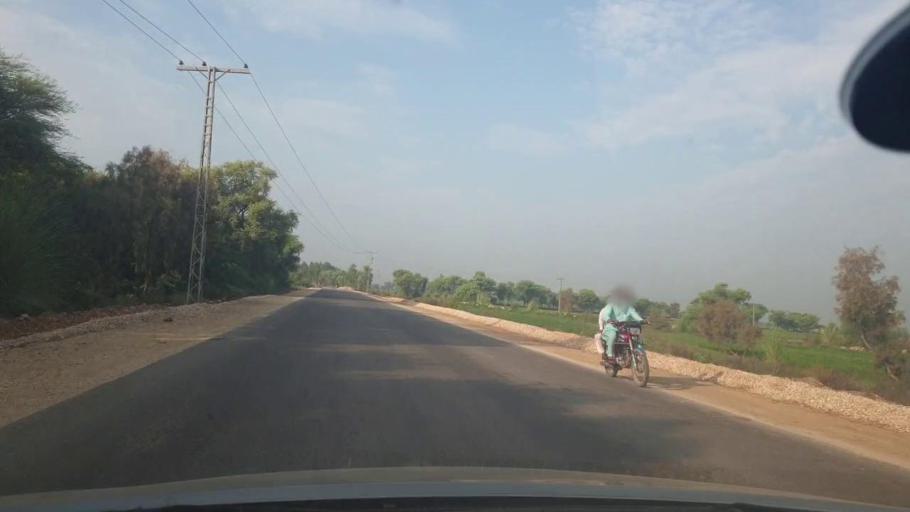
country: PK
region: Sindh
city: Jacobabad
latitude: 28.2433
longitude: 68.3948
